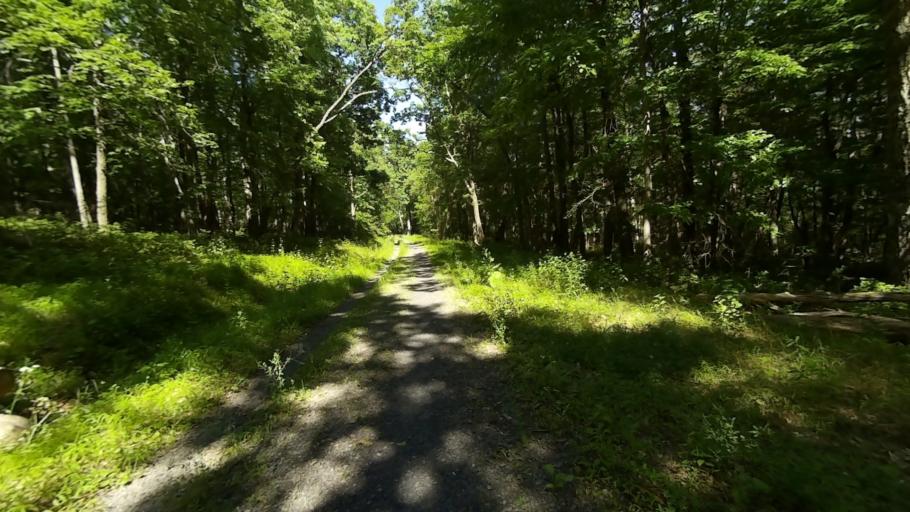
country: US
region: Pennsylvania
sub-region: Centre County
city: Boalsburg
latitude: 40.7362
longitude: -77.7641
